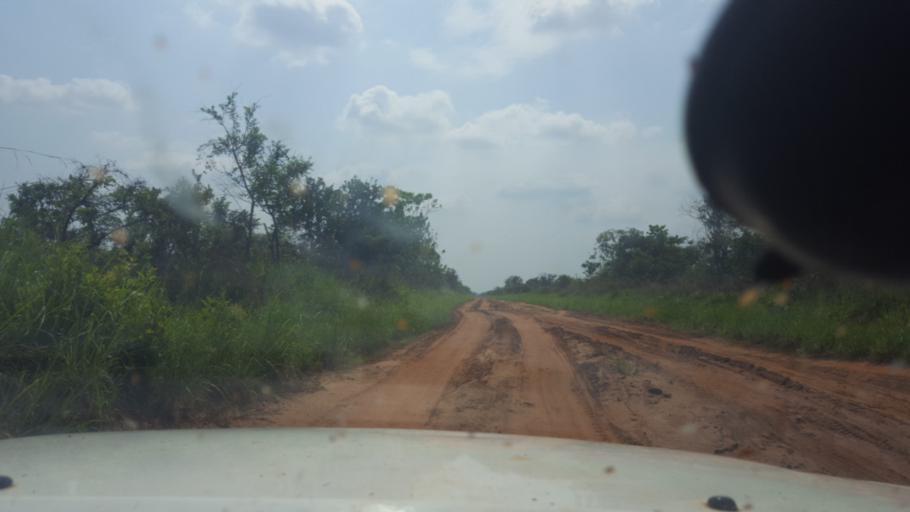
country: CD
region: Bandundu
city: Bandundu
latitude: -3.7619
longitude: 17.1416
